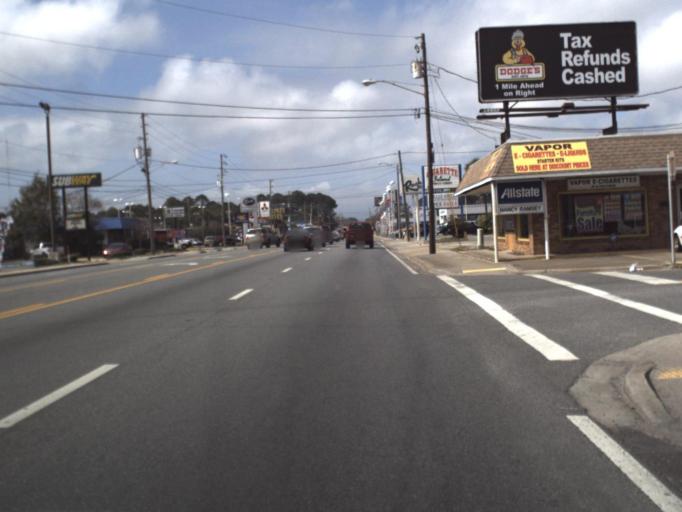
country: US
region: Florida
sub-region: Bay County
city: Panama City
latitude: 30.1752
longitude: -85.6646
